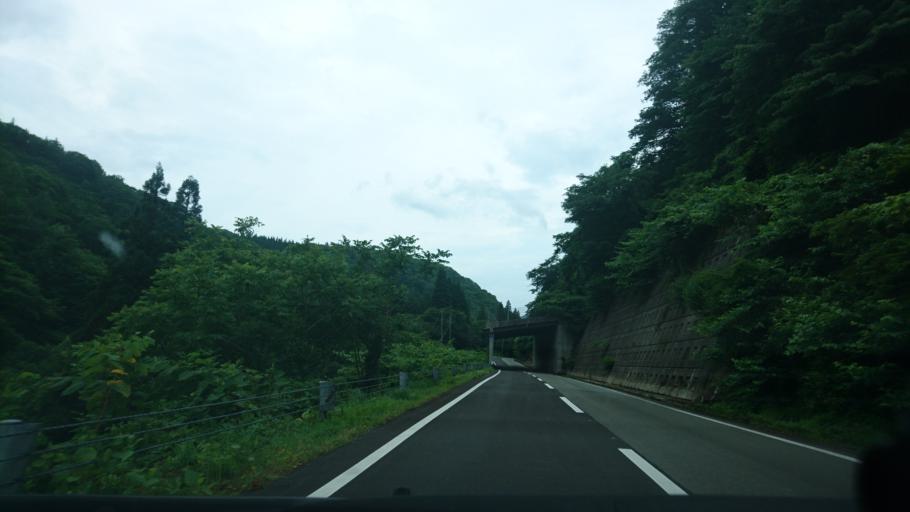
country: JP
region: Akita
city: Yuzawa
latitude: 39.1675
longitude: 140.7404
